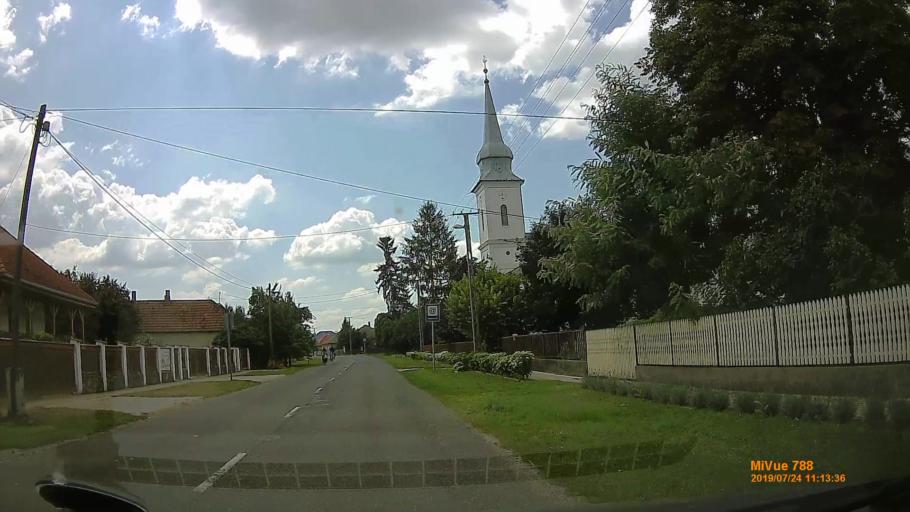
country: HU
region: Szabolcs-Szatmar-Bereg
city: Tarpa
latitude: 48.2012
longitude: 22.4451
